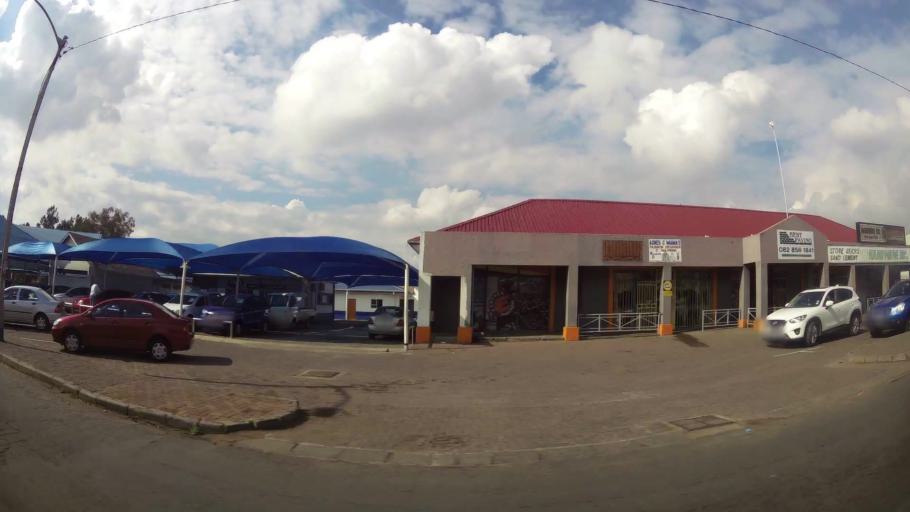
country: ZA
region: Gauteng
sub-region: Sedibeng District Municipality
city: Vereeniging
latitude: -26.6694
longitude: 27.9350
